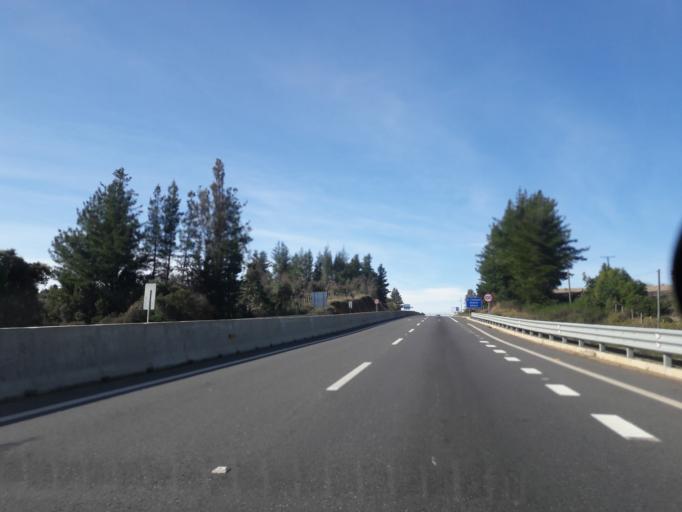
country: CL
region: Biobio
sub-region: Provincia de Biobio
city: Yumbel
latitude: -36.9627
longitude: -72.7143
